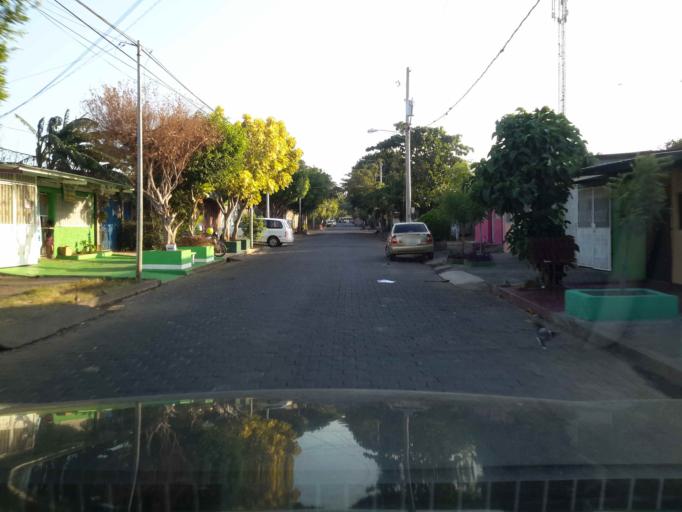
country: NI
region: Managua
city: Ciudad Sandino
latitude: 12.1571
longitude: -86.2997
